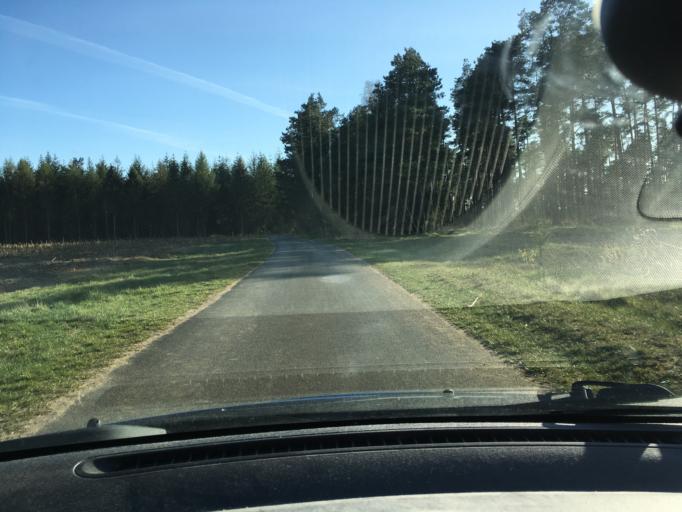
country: DE
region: Lower Saxony
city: Bispingen
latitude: 53.1100
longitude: 10.0123
